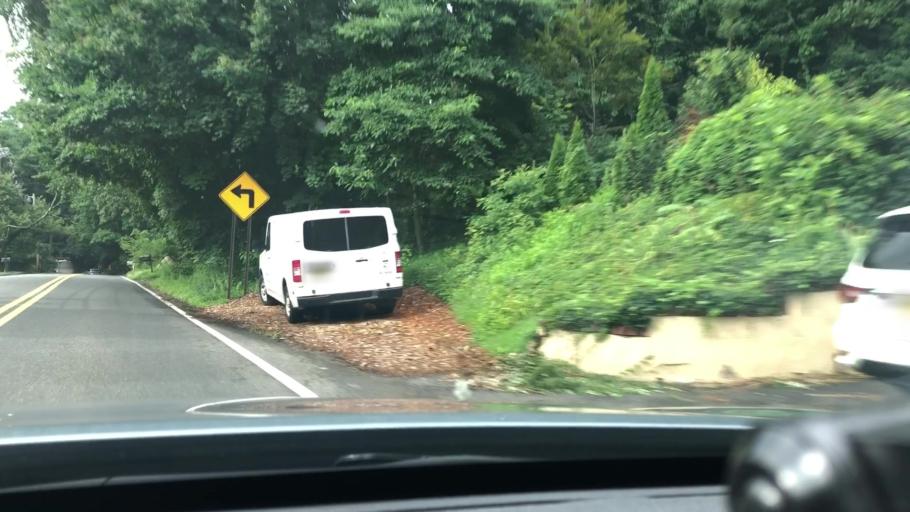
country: US
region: New Jersey
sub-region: Bergen County
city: Woodcliff Lake
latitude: 41.0031
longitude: -74.0750
